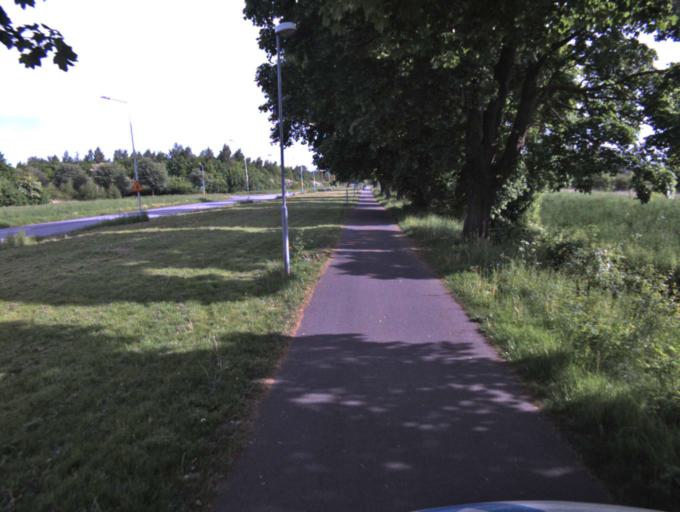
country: SE
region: Skane
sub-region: Kristianstads Kommun
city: Kristianstad
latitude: 56.0332
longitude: 14.1862
